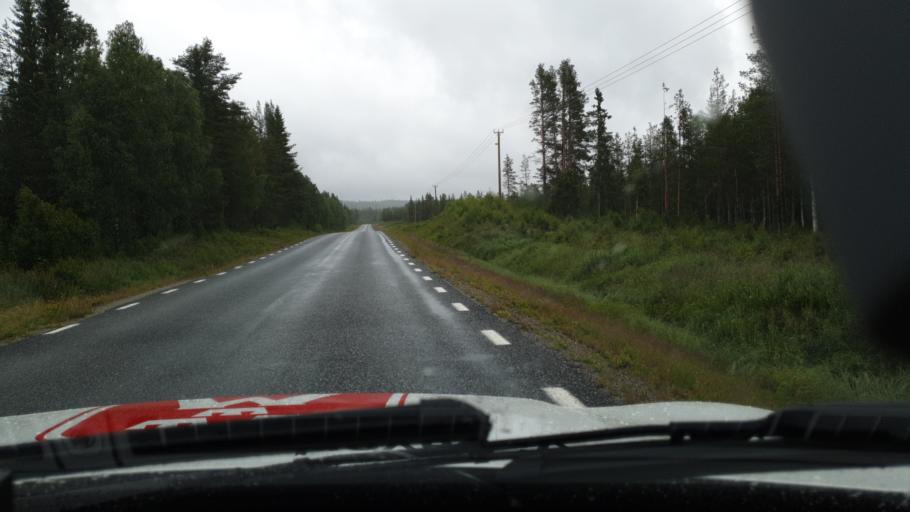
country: SE
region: Vaesterbotten
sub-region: Asele Kommun
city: Insjon
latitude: 64.3107
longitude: 17.6953
